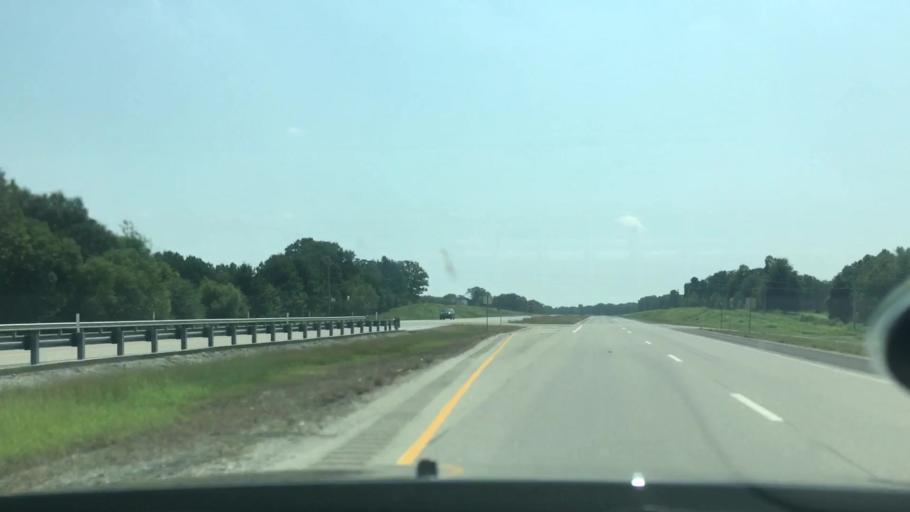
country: US
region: Oklahoma
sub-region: Atoka County
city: Atoka
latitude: 34.3238
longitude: -96.0411
